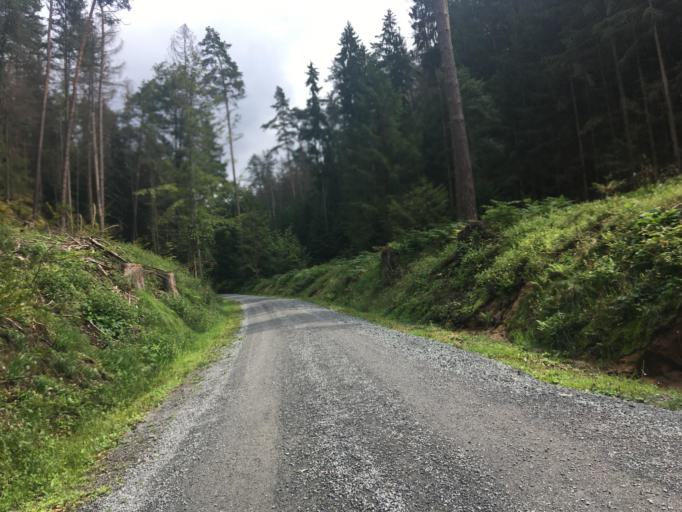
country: DE
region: Saxony
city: Bad Schandau
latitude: 50.9207
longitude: 14.1949
